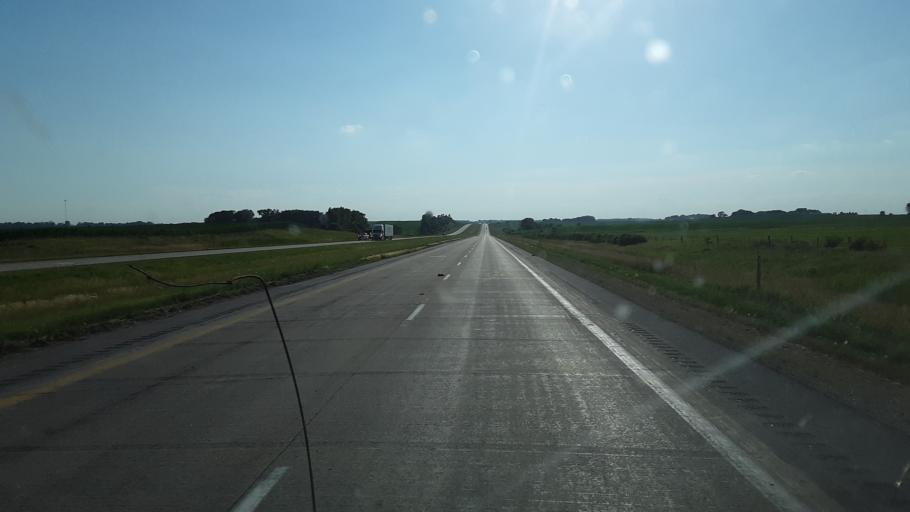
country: US
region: Iowa
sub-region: Hardin County
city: Iowa Falls
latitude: 42.4483
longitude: -93.3010
